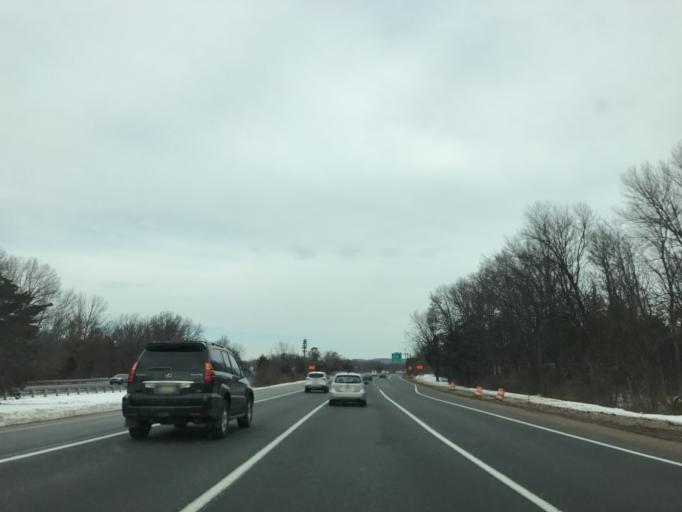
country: US
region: New Jersey
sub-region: Somerset County
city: Bedminster
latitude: 40.6548
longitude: -74.6455
